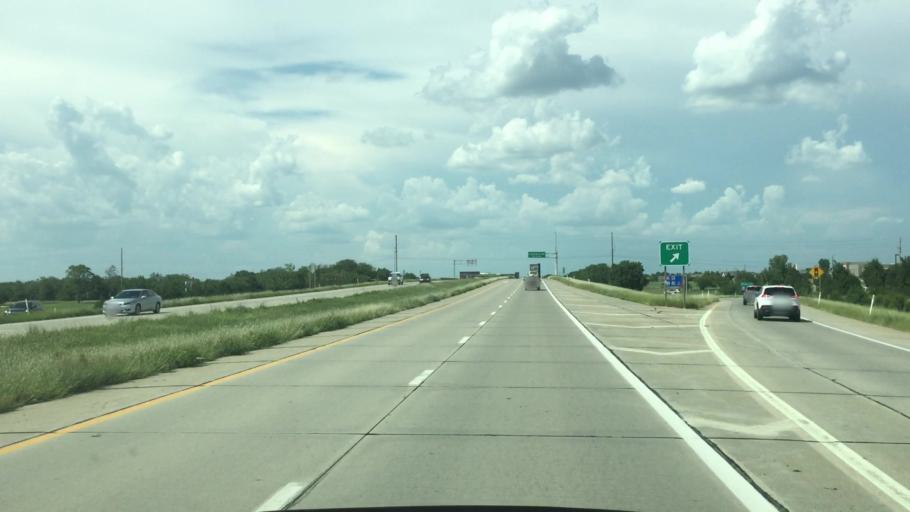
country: US
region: Kansas
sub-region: Butler County
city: Andover
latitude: 37.7204
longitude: -97.1994
